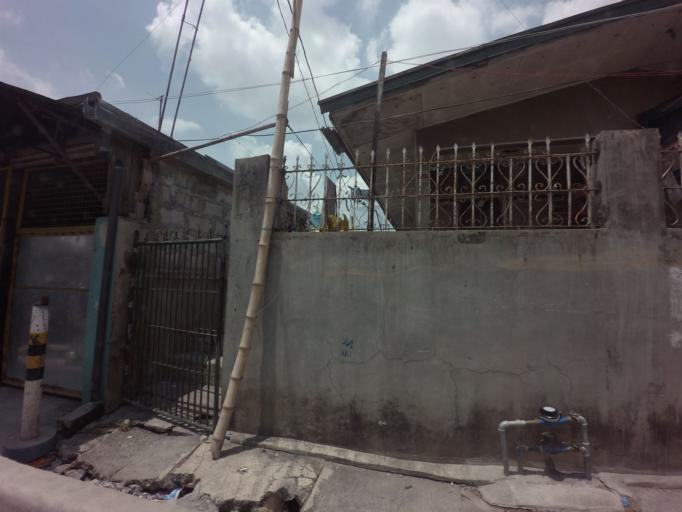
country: PH
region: Calabarzon
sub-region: Province of Laguna
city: San Pedro
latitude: 14.3905
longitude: 121.0507
